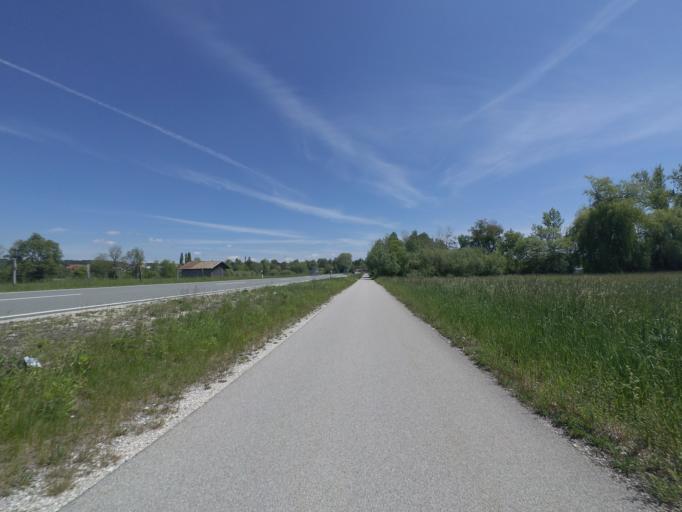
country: DE
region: Bavaria
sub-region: Upper Bavaria
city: Taching am See
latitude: 47.9541
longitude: 12.7446
